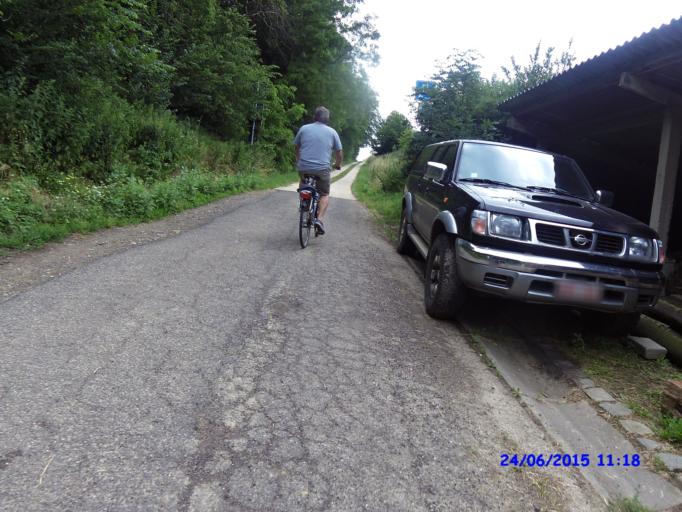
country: BE
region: Flanders
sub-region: Provincie Limburg
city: Borgloon
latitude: 50.7913
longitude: 5.3171
